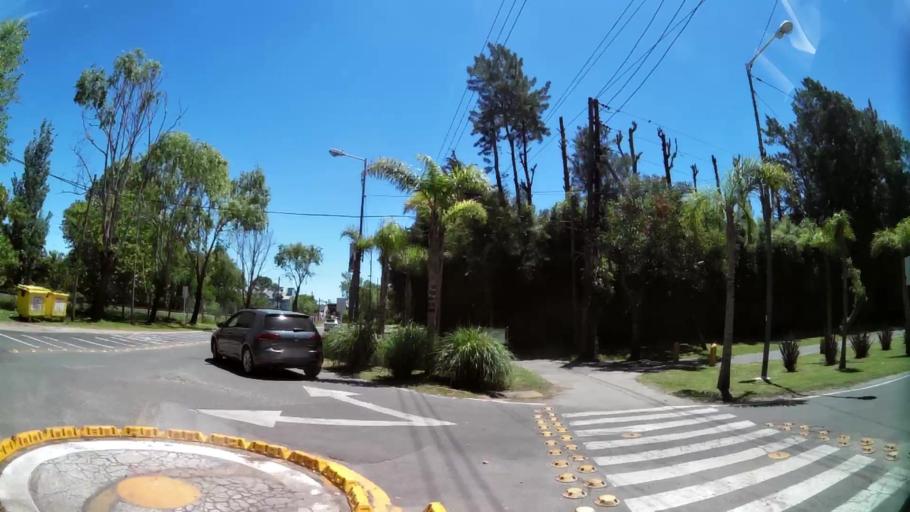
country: AR
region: Buenos Aires
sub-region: Partido de Tigre
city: Tigre
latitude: -34.4439
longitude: -58.5413
